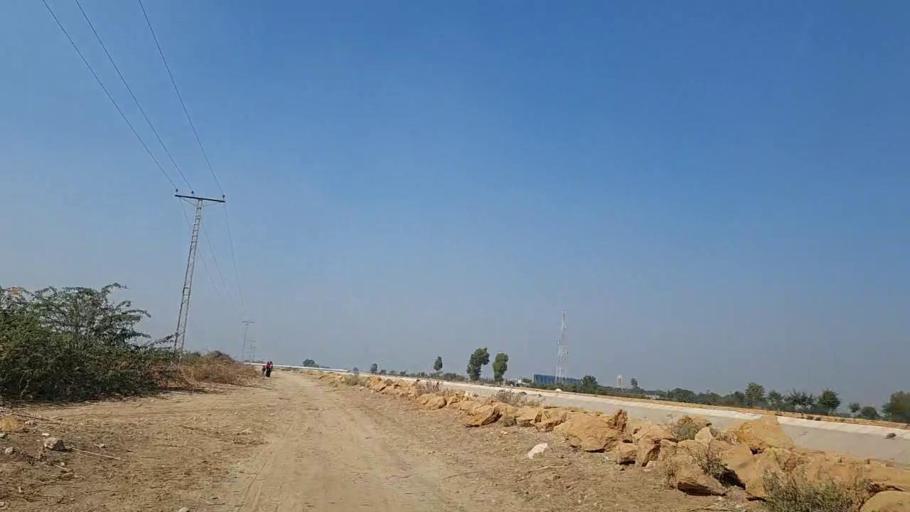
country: PK
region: Sindh
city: Sakrand
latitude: 26.2416
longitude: 68.2713
